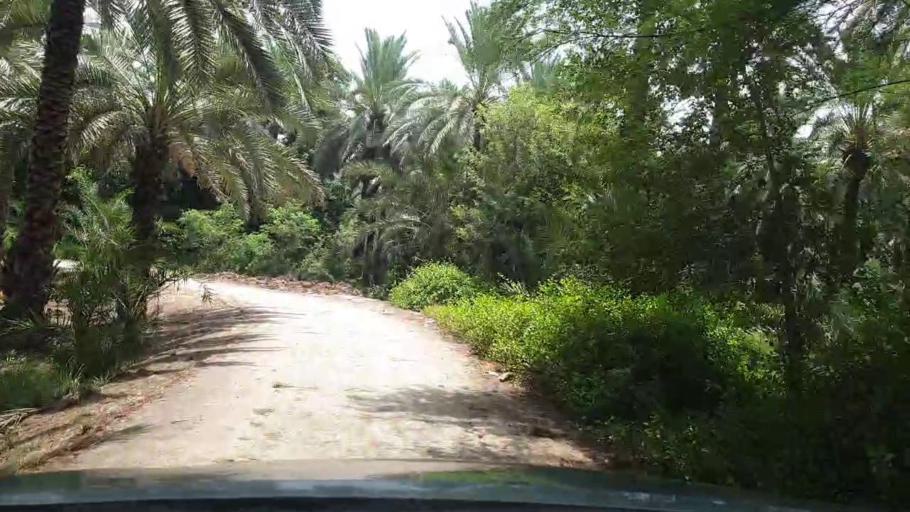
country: PK
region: Sindh
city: Khairpur
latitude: 27.6349
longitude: 68.7307
